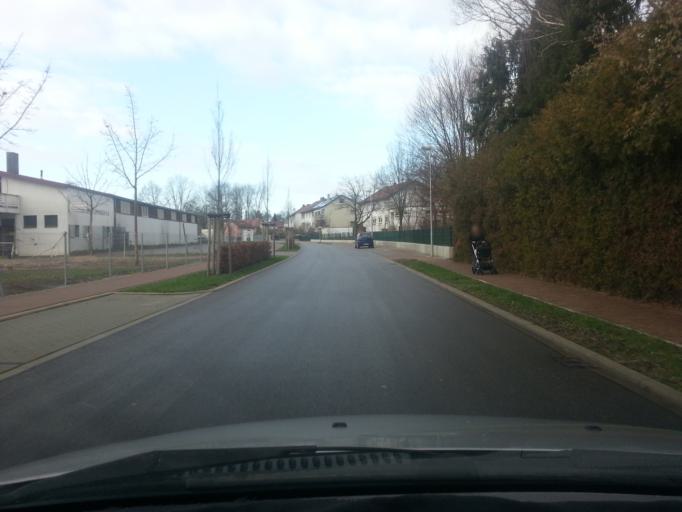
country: DE
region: Baden-Wuerttemberg
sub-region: Regierungsbezirk Stuttgart
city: Eppingen
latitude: 49.1412
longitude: 8.9061
